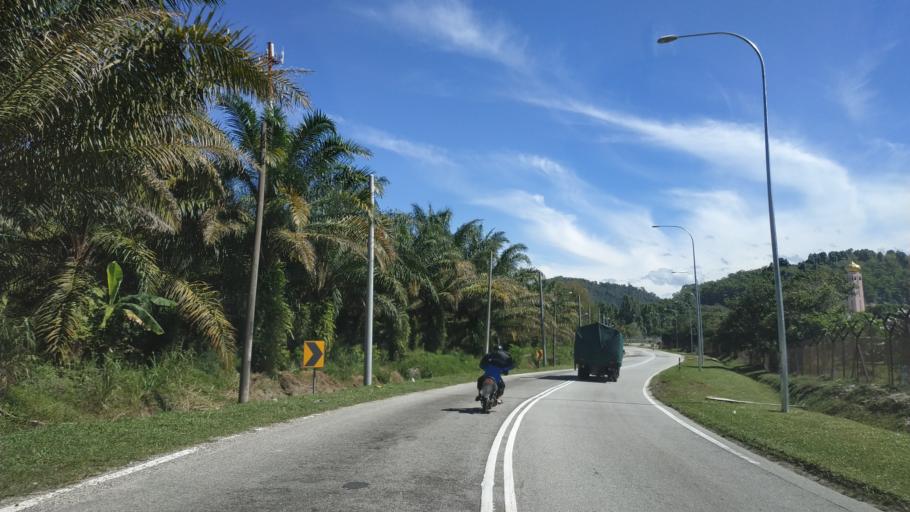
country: MY
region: Kedah
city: Kulim
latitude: 5.3336
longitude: 100.5353
